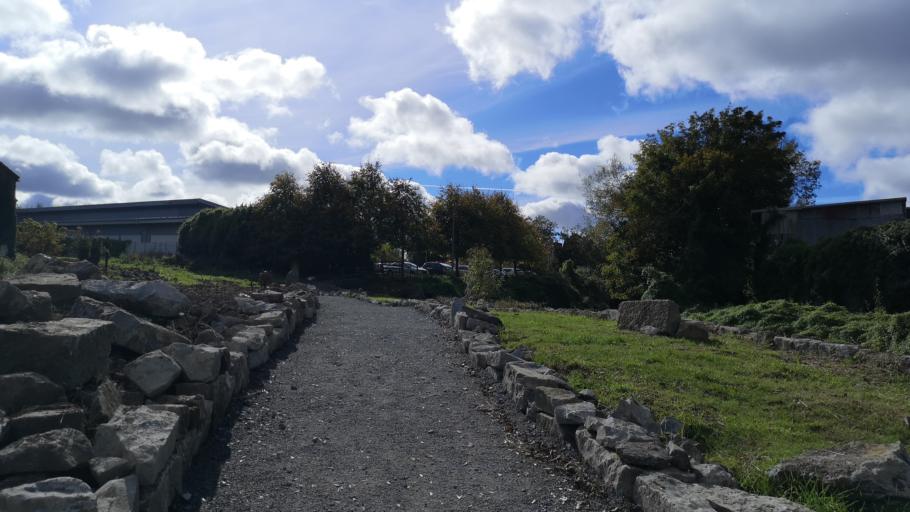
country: IE
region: Connaught
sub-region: County Galway
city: Gort
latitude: 53.0676
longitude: -8.8164
